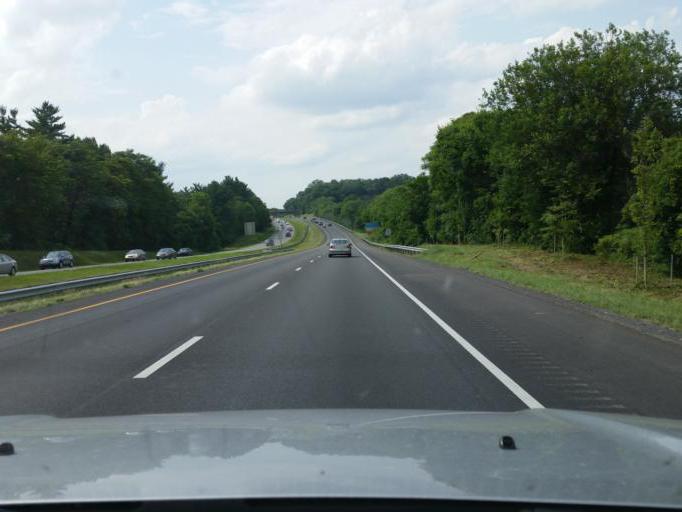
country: US
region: Maryland
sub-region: Frederick County
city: Urbana
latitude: 39.3303
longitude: -77.3722
